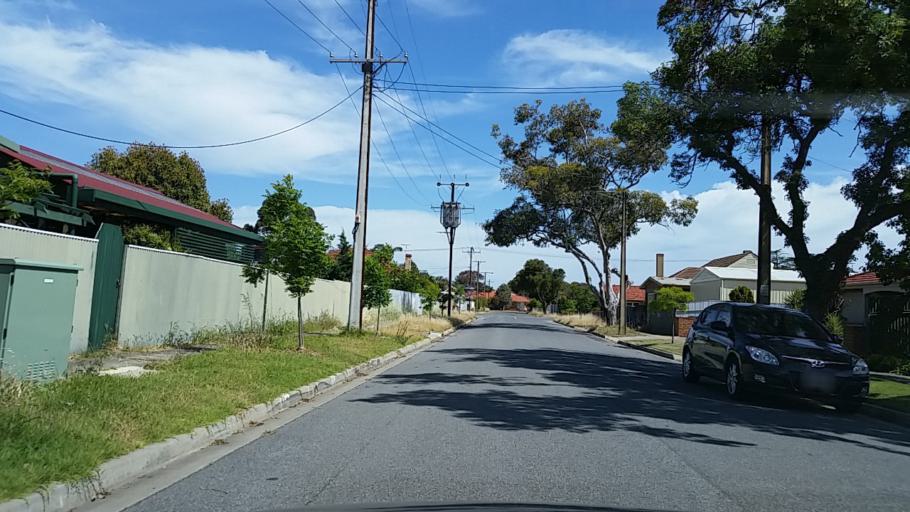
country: AU
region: South Australia
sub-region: Charles Sturt
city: Royal Park
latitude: -34.8864
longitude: 138.5161
